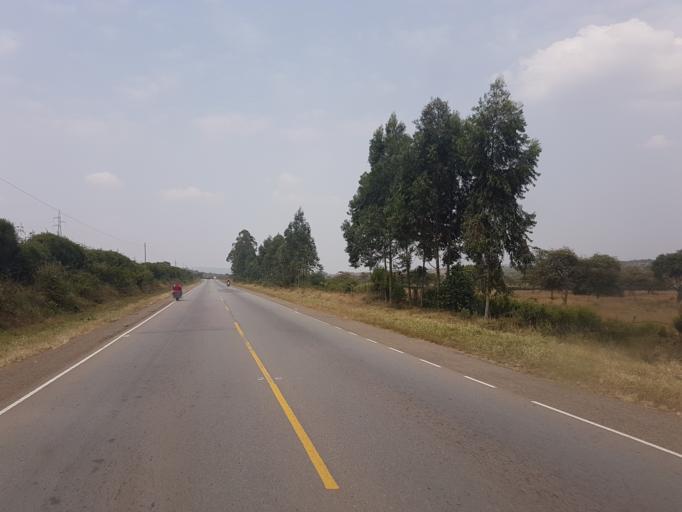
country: UG
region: Western Region
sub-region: Mbarara District
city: Mbarara
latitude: -0.5105
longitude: 30.7879
